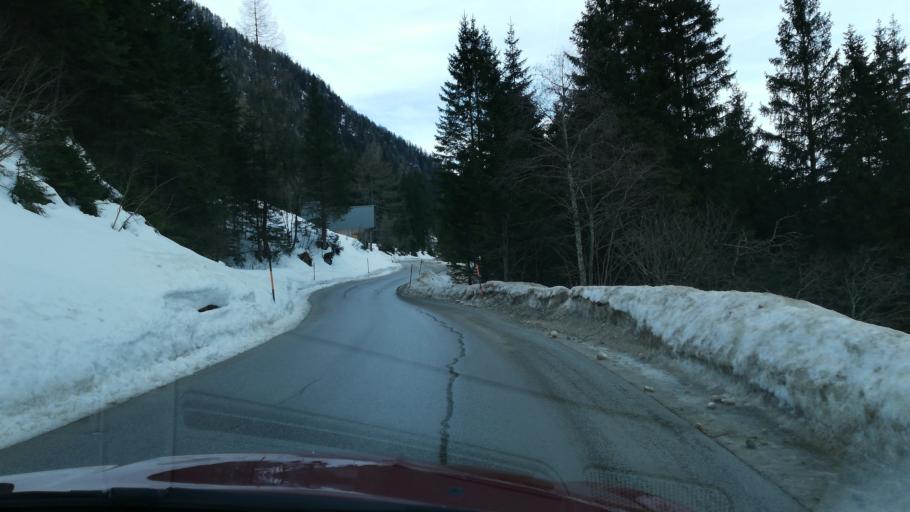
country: AT
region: Styria
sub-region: Politischer Bezirk Liezen
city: Donnersbach
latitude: 47.4167
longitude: 14.1728
